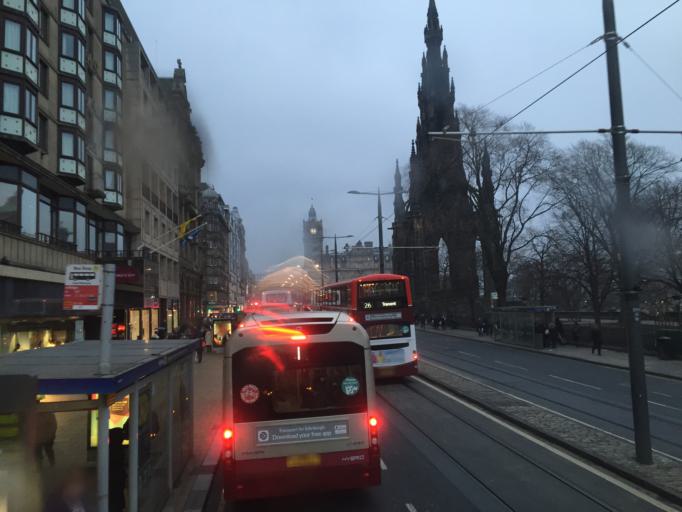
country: GB
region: Scotland
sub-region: Edinburgh
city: Edinburgh
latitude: 55.9524
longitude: -3.1949
